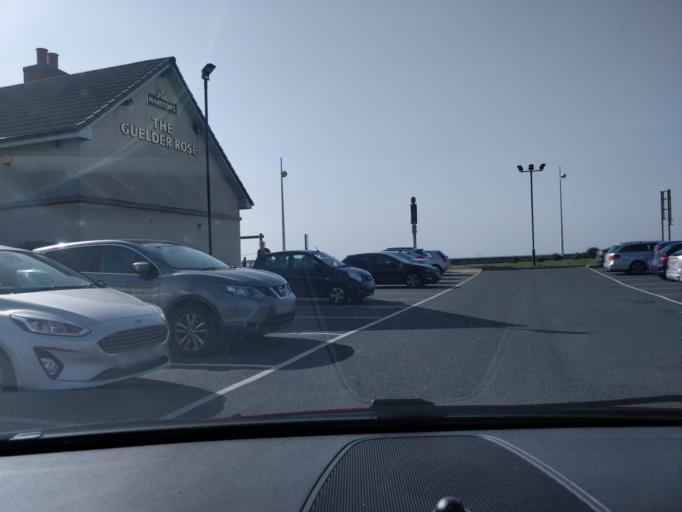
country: GB
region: England
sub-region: Sefton
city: Southport
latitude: 53.6535
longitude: -3.0132
